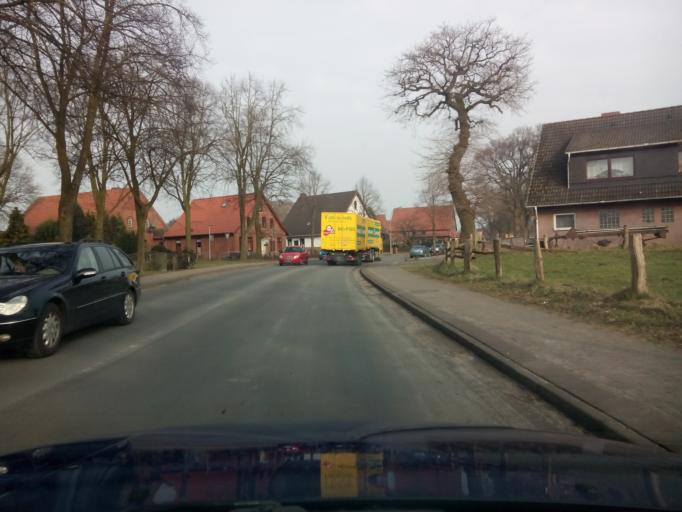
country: DE
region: Lower Saxony
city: Langen
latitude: 53.6206
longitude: 8.6352
